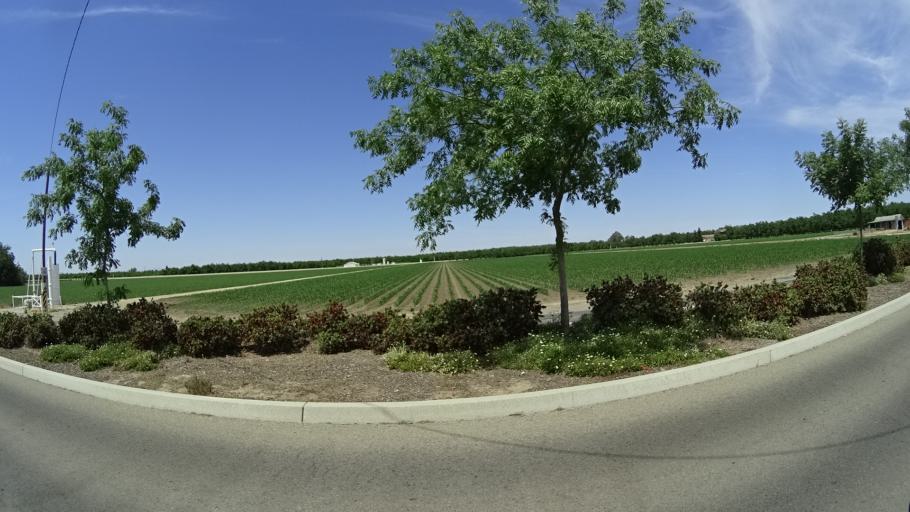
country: US
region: California
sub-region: Kings County
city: Armona
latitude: 36.3337
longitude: -119.6910
